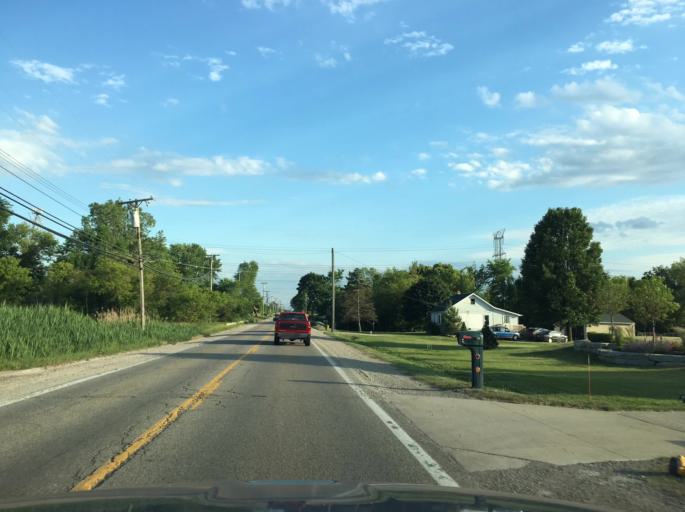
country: US
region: Michigan
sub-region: Macomb County
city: Shelby
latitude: 42.7260
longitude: -82.9599
